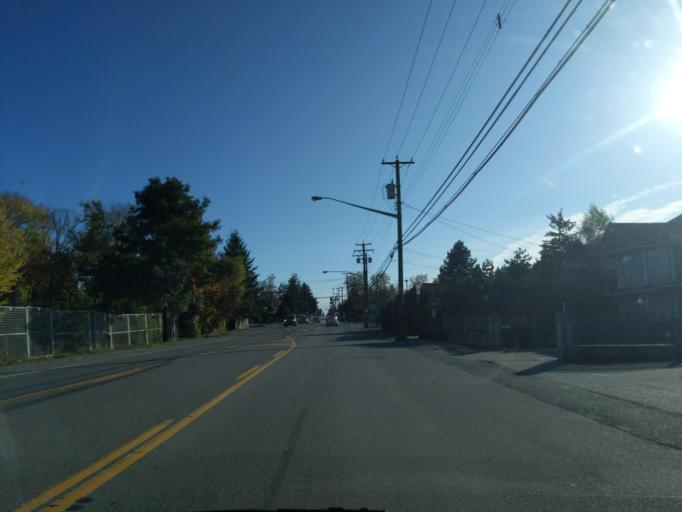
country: CA
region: British Columbia
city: New Westminster
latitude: 49.2001
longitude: -122.8565
